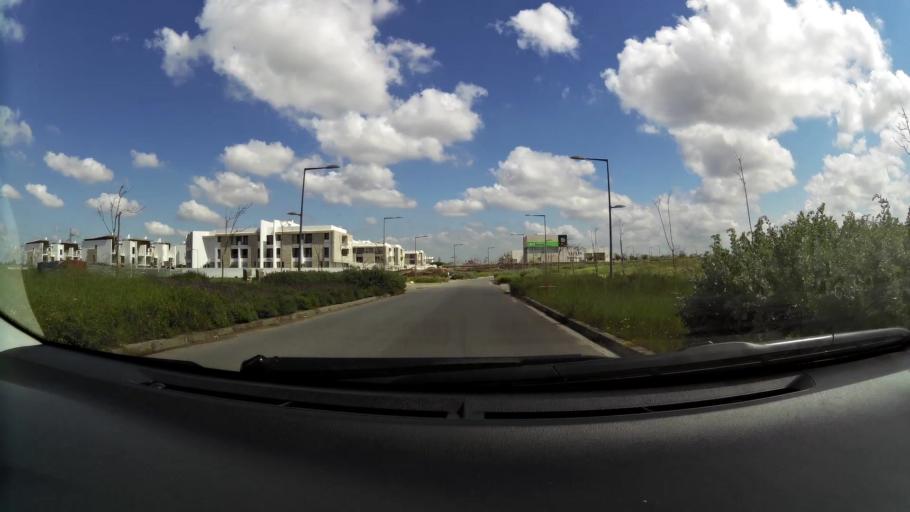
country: MA
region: Grand Casablanca
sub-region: Nouaceur
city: Bouskoura
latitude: 33.4955
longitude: -7.6044
